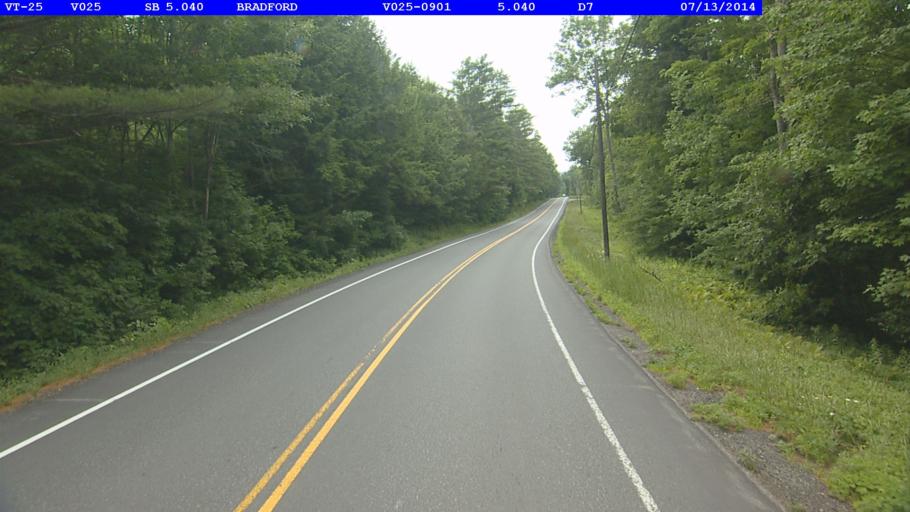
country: US
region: New Hampshire
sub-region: Grafton County
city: Haverhill
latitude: 44.0250
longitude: -72.1750
